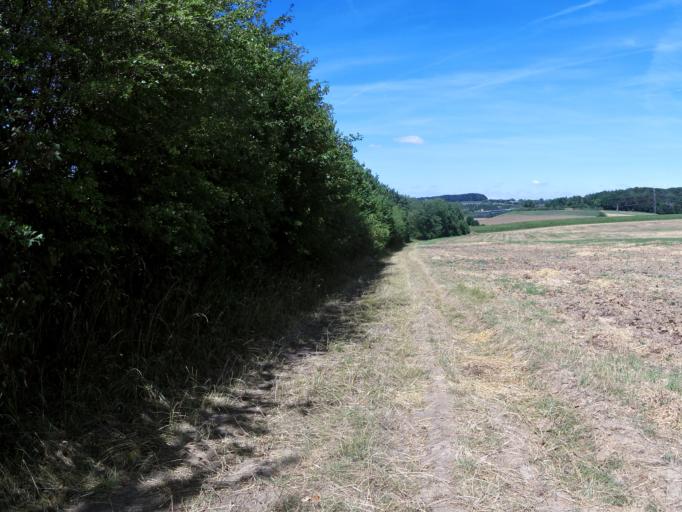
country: DE
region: Bavaria
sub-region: Regierungsbezirk Unterfranken
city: Hettstadt
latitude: 49.8094
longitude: 9.8085
